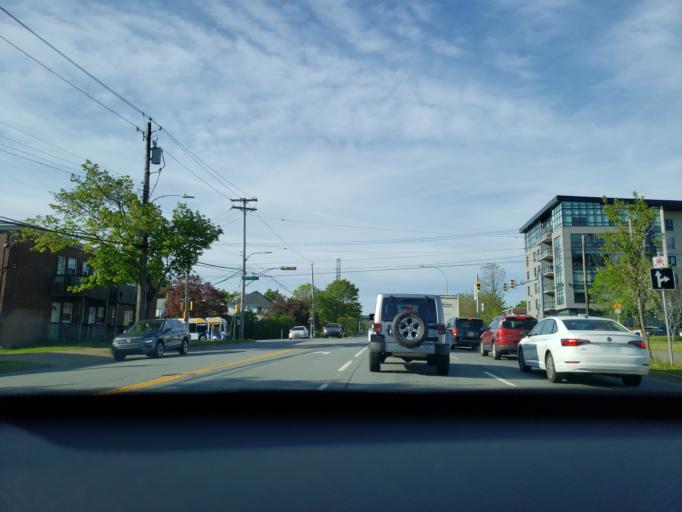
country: CA
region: Nova Scotia
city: Dartmouth
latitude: 44.6543
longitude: -63.6301
